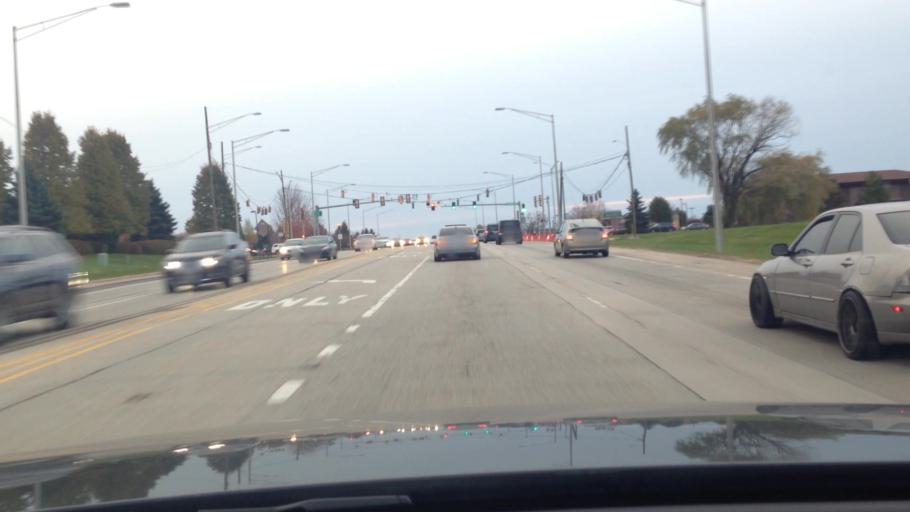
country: US
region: Illinois
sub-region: McHenry County
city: Lake in the Hills
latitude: 42.1670
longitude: -88.3353
